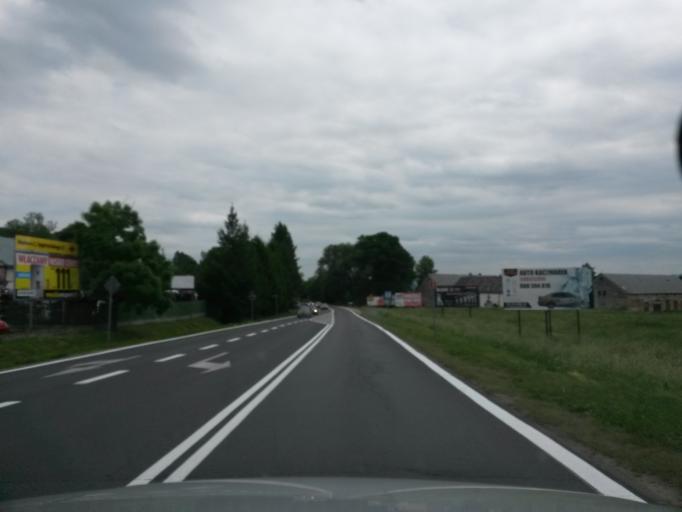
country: PL
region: Lower Silesian Voivodeship
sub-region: Jelenia Gora
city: Cieplice Slaskie Zdroj
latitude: 50.8924
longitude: 15.6827
